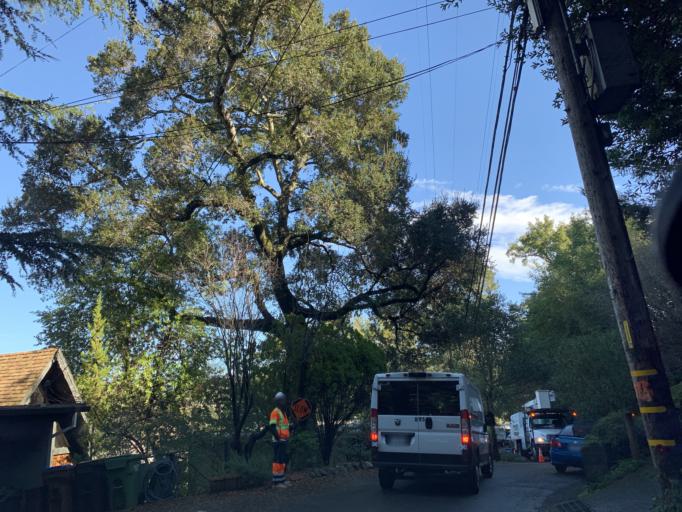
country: US
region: California
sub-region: Marin County
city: Strawberry
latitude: 37.9033
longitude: -122.5224
